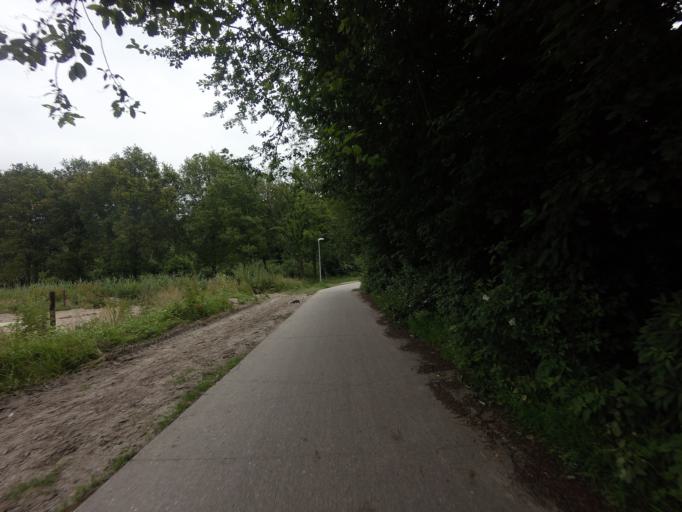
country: NL
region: Flevoland
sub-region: Gemeente Almere
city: Almere Stad
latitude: 52.3785
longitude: 5.2861
